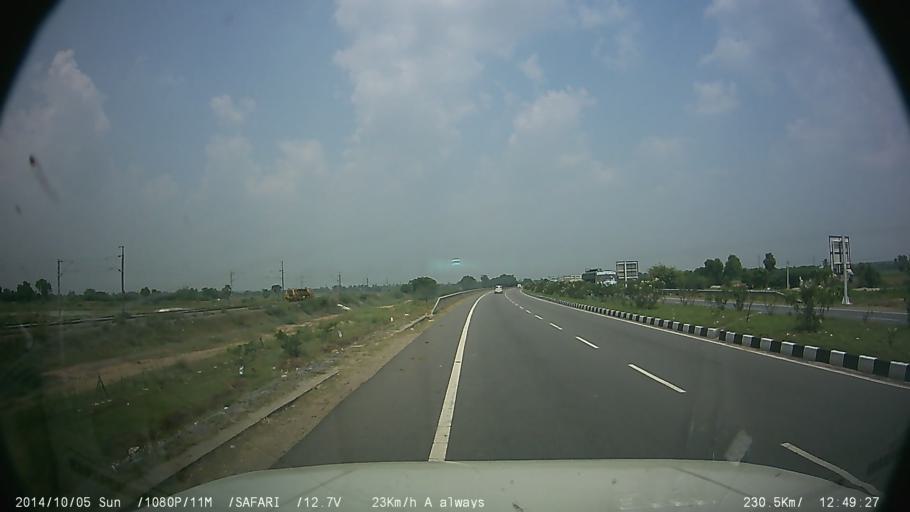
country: IN
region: Tamil Nadu
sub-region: Cuddalore
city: Vriddhachalam
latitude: 11.7089
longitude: 79.3242
